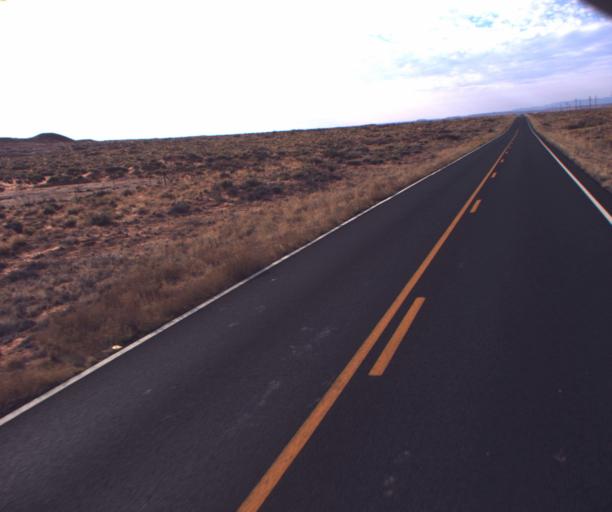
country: US
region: Arizona
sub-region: Apache County
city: Many Farms
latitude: 36.8694
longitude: -109.6327
